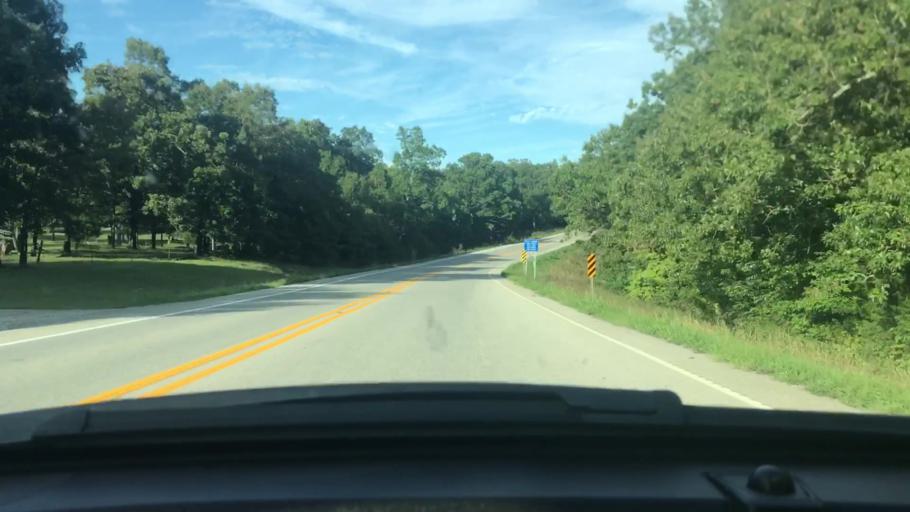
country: US
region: Arkansas
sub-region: Sharp County
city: Cherokee Village
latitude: 36.2759
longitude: -91.3156
